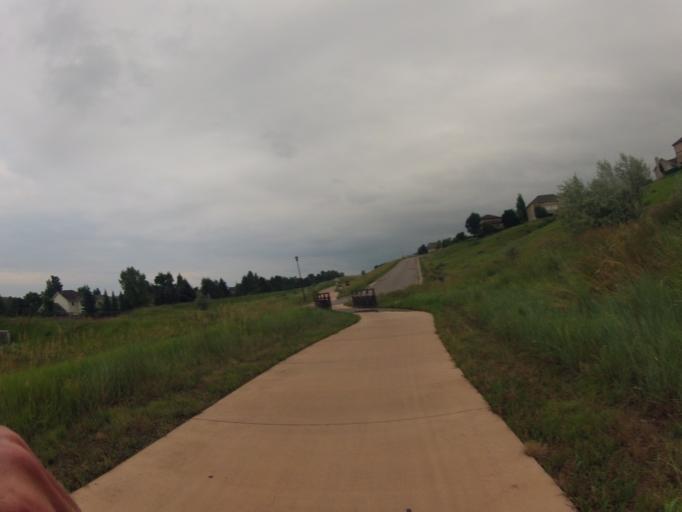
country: US
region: Colorado
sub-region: Larimer County
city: Fort Collins
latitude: 40.5279
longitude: -105.1253
